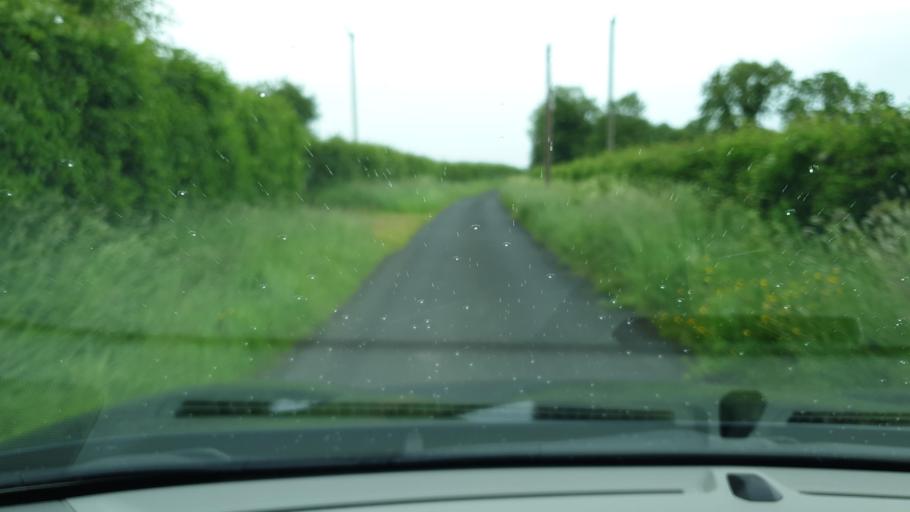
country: IE
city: Confey
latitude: 53.4294
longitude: -6.5324
